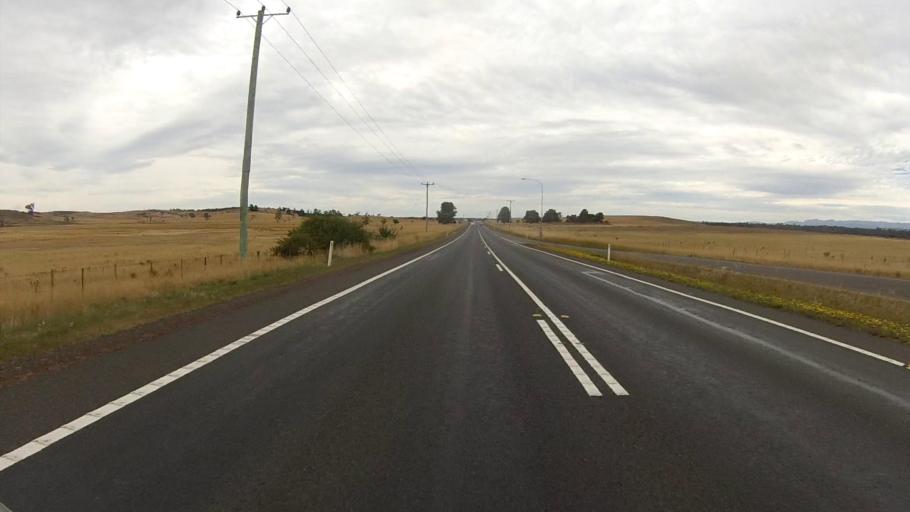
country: AU
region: Tasmania
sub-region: Northern Midlands
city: Evandale
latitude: -41.8839
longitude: 147.4666
